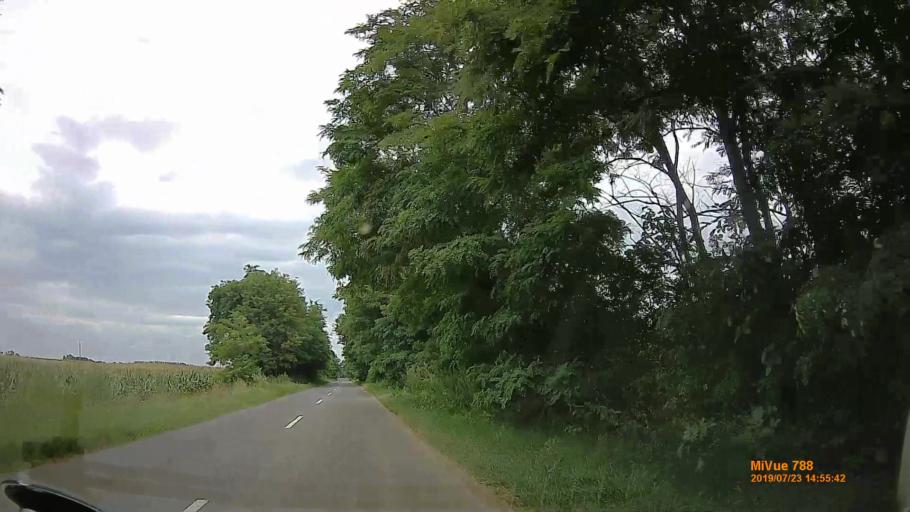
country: HU
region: Szabolcs-Szatmar-Bereg
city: Kalmanhaza
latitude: 47.8933
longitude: 21.6607
